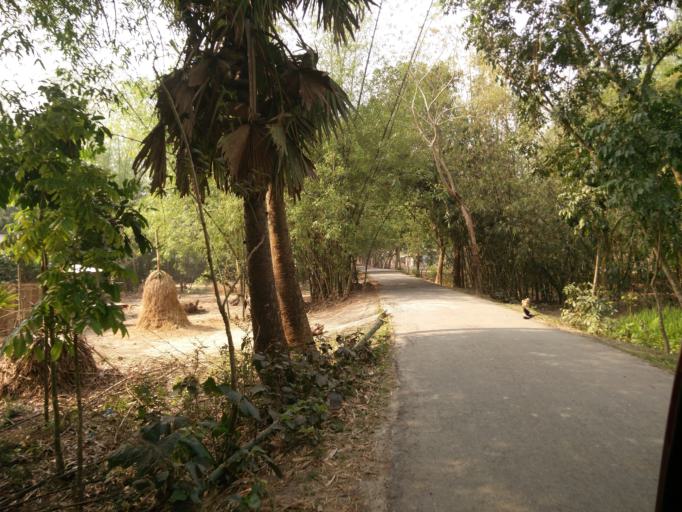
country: BD
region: Dhaka
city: Sherpur
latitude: 24.9141
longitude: 90.1565
